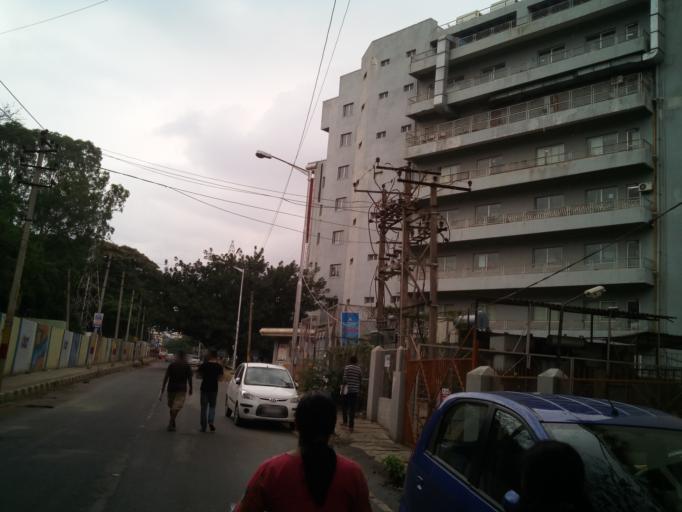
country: IN
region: Karnataka
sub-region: Bangalore Urban
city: Bangalore
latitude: 12.9909
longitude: 77.6590
